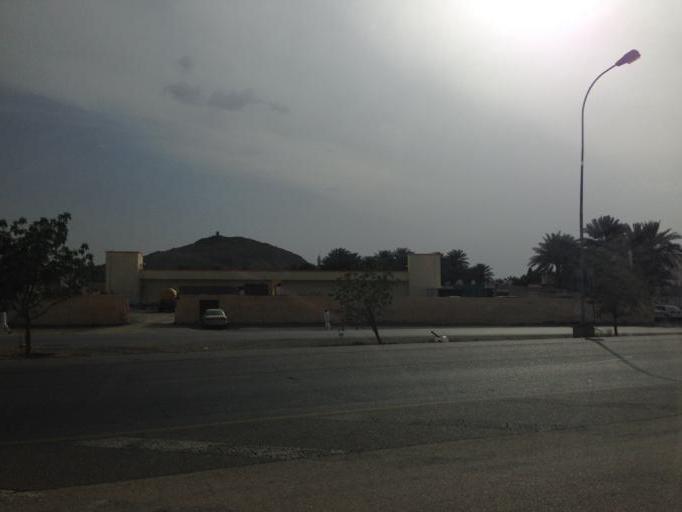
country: OM
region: Ash Sharqiyah
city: Al Qabil
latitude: 22.5832
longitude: 58.6875
